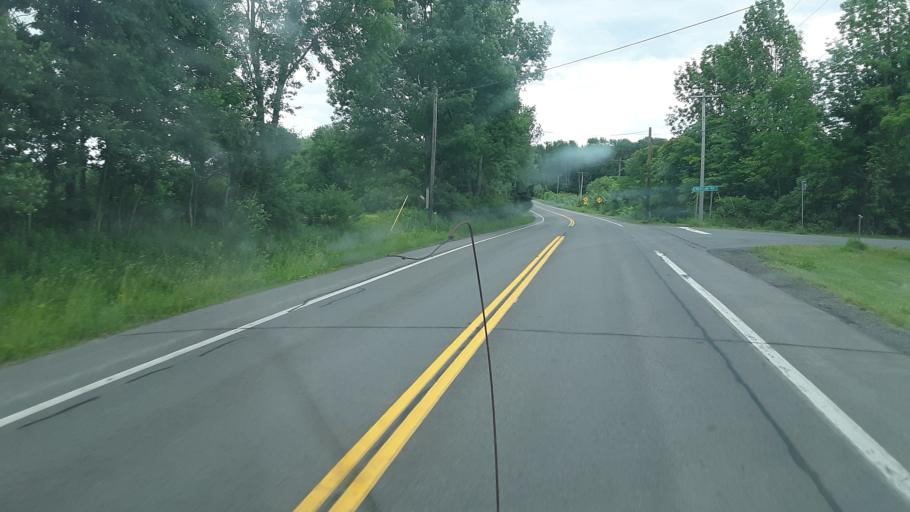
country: US
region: New York
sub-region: Oneida County
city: Rome
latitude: 43.3279
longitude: -75.4770
